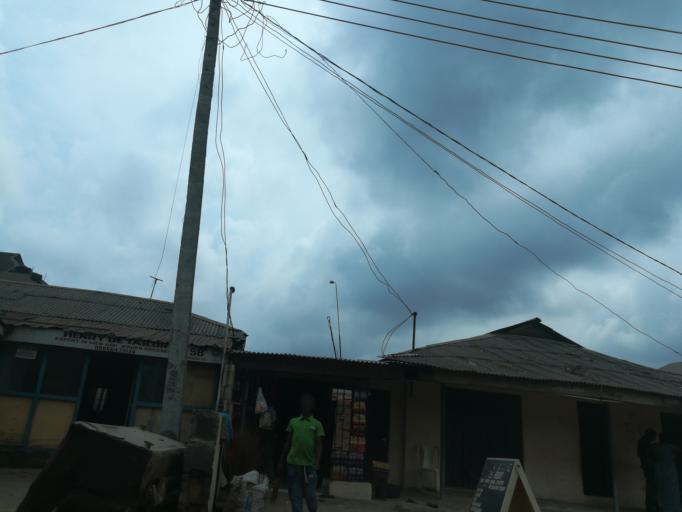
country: NG
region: Lagos
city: Oshodi
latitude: 6.5608
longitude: 3.3449
